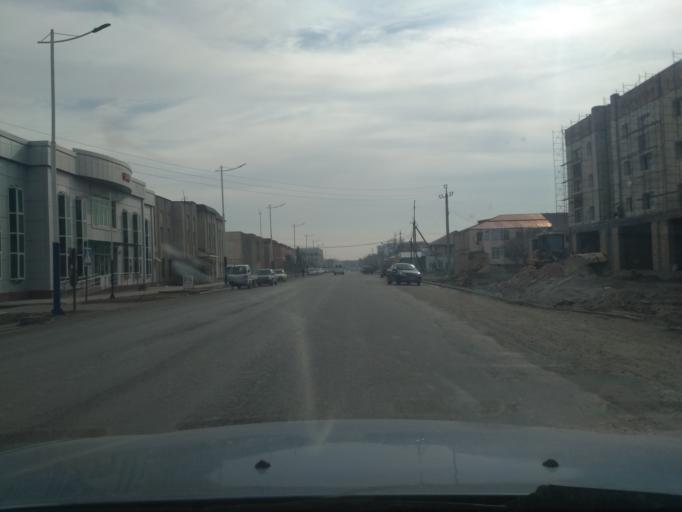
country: UZ
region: Sirdaryo
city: Guliston
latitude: 40.5014
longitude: 68.7719
